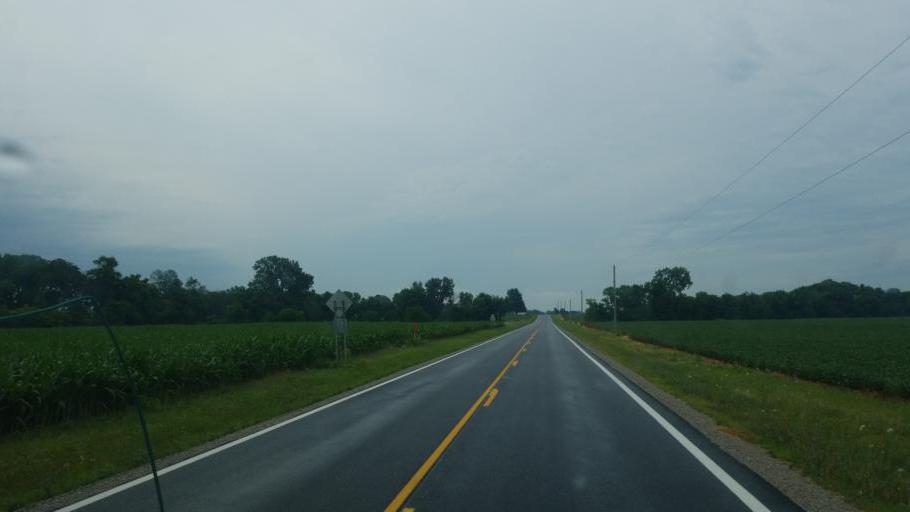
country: US
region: Ohio
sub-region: Williams County
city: Edgerton
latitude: 41.3813
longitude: -84.6697
